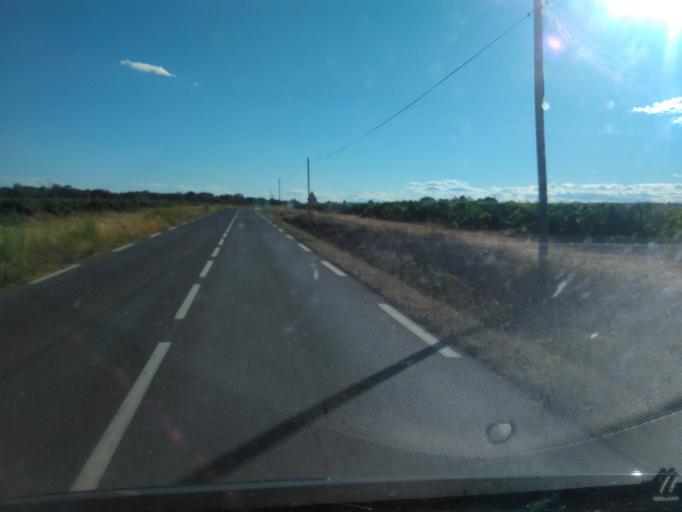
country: FR
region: Languedoc-Roussillon
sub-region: Departement du Gard
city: Saint-Gilles
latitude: 43.6680
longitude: 4.3807
